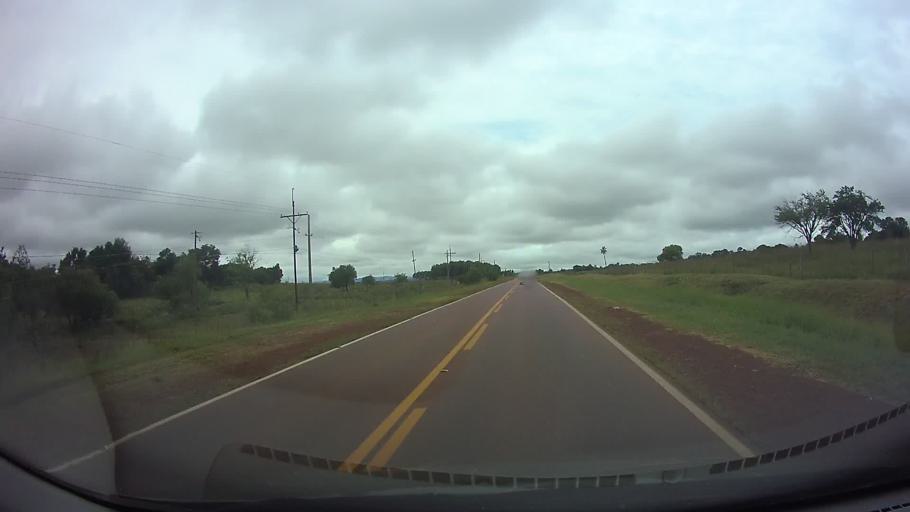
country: PY
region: Paraguari
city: Carapegua
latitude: -25.8033
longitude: -57.1887
